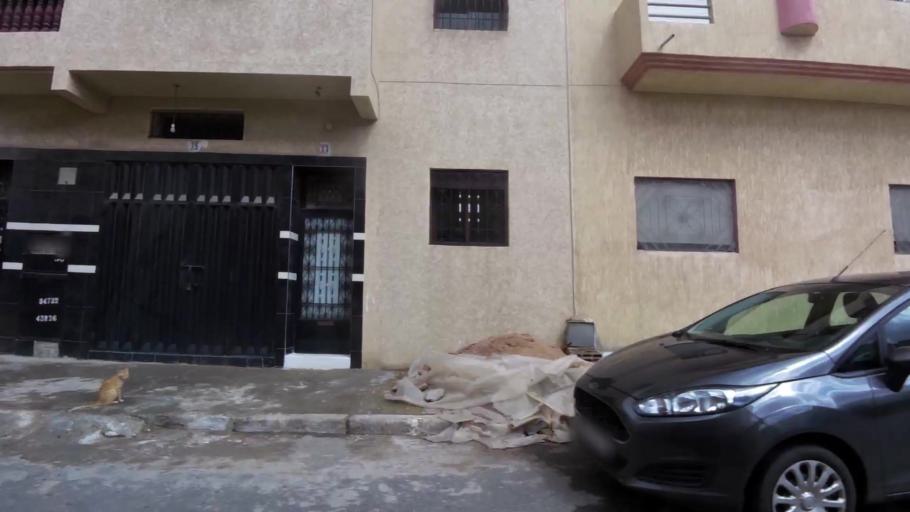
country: MA
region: Chaouia-Ouardigha
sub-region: Settat Province
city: Berrechid
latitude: 33.2750
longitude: -7.5906
